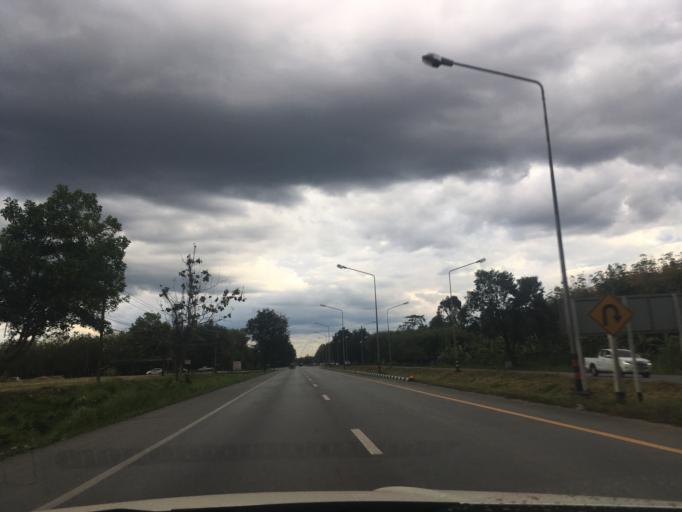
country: TH
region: Chon Buri
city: Nong Yai
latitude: 13.0771
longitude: 101.4073
